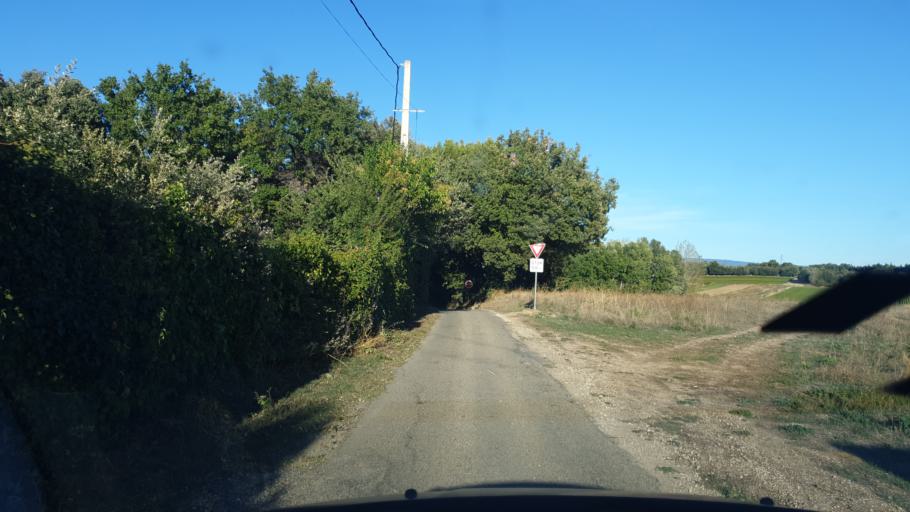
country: FR
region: Provence-Alpes-Cote d'Azur
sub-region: Departement du Vaucluse
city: Loriol-du-Comtat
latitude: 44.0560
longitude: 5.0036
